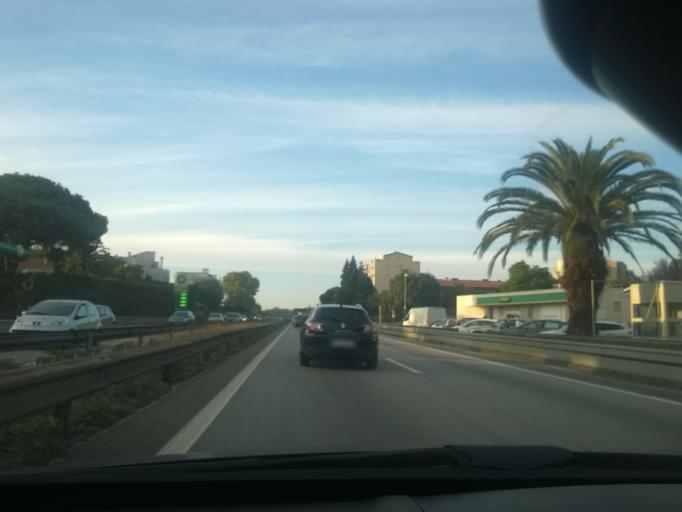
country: PT
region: Porto
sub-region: Matosinhos
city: Sao Mamede de Infesta
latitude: 41.1861
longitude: -8.6246
